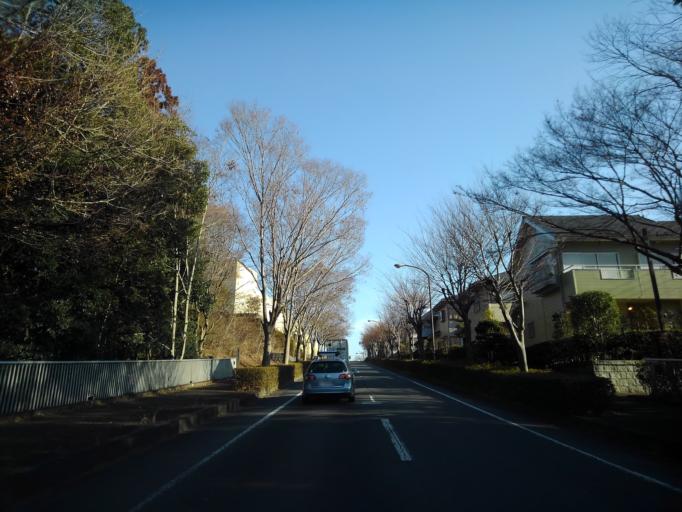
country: JP
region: Saitama
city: Hanno
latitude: 35.8400
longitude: 139.3094
